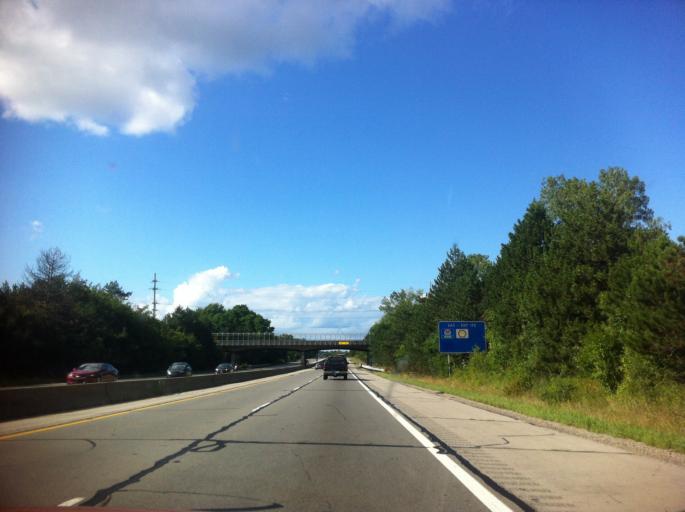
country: US
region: Michigan
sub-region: Washtenaw County
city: Ann Arbor
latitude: 42.2540
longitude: -83.7745
